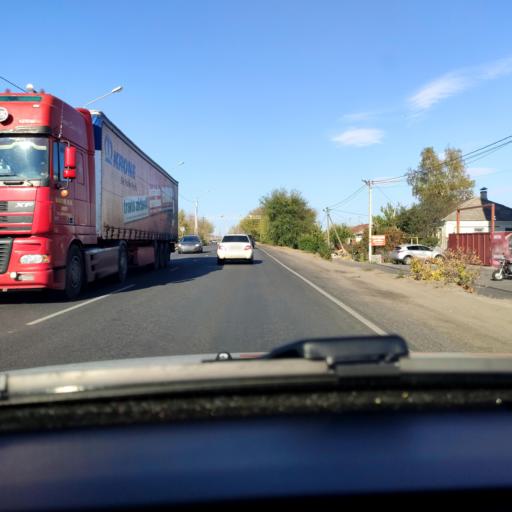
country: RU
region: Voronezj
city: Pridonskoy
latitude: 51.7124
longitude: 39.0745
